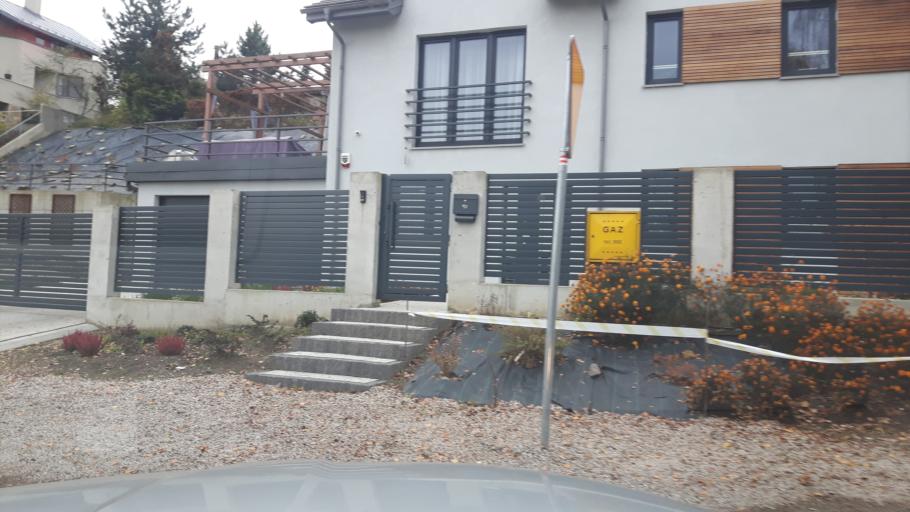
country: PL
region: Masovian Voivodeship
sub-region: Warszawa
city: Ursynow
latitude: 52.1556
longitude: 21.0605
